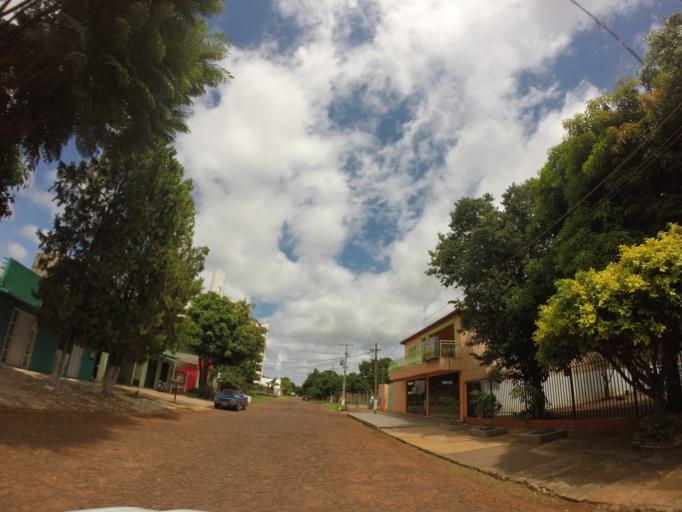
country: PY
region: Alto Parana
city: Ciudad del Este
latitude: -25.4060
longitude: -54.6327
